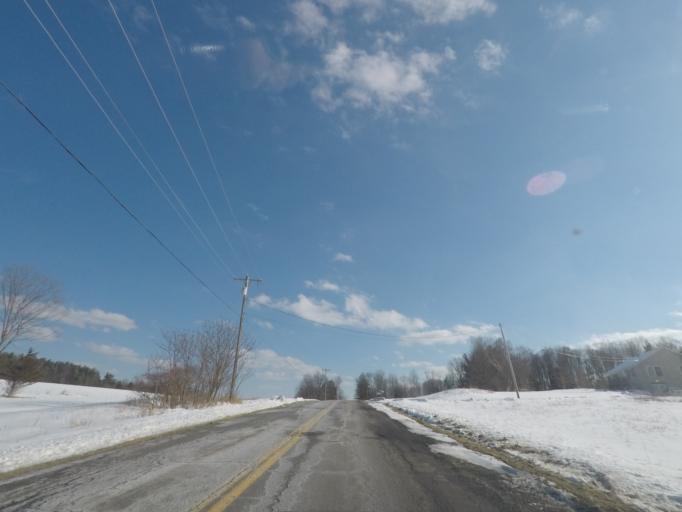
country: US
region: New York
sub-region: Rensselaer County
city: Hoosick Falls
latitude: 42.8513
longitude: -73.4923
